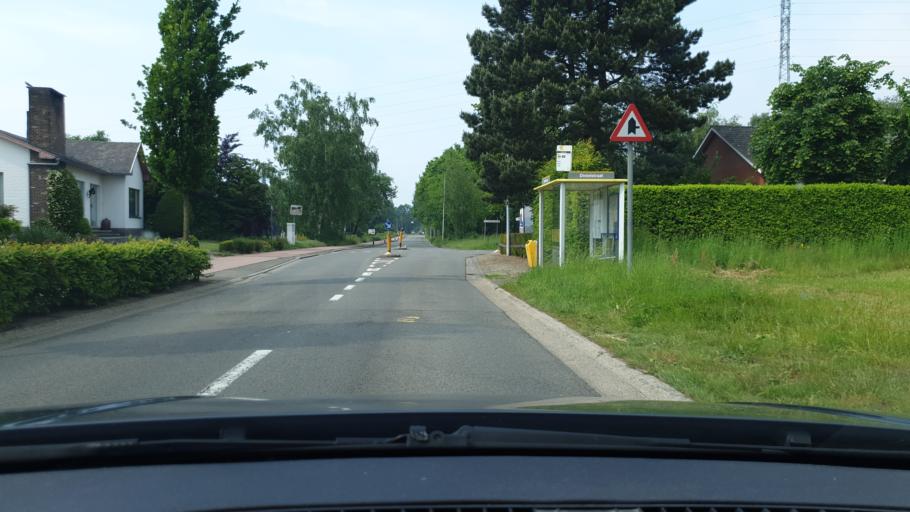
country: BE
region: Flanders
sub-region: Provincie Antwerpen
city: Olen
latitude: 51.1725
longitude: 4.8916
